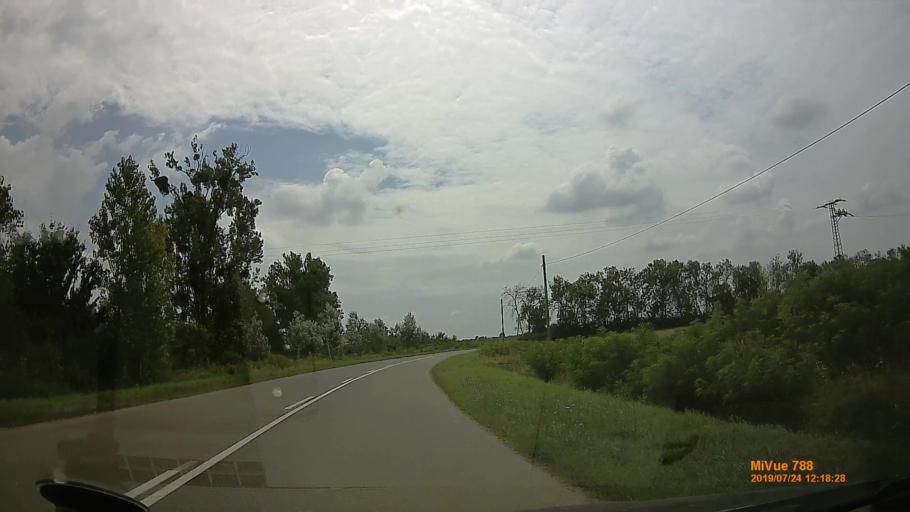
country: HU
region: Szabolcs-Szatmar-Bereg
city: Vasarosnameny
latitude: 48.1506
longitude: 22.3481
